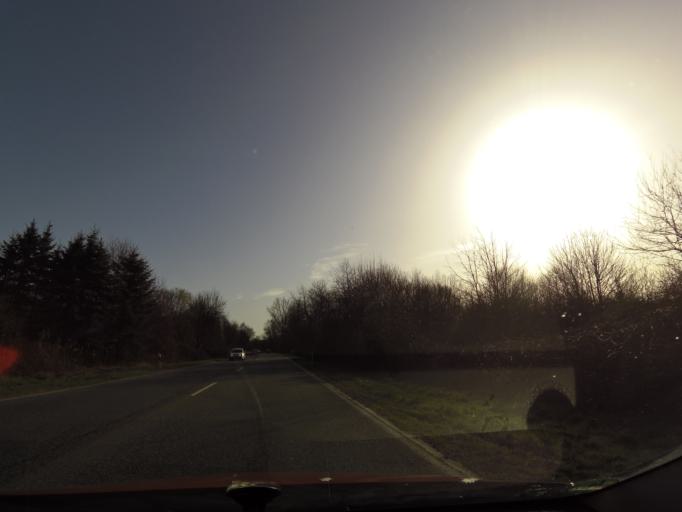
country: DE
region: Rheinland-Pfalz
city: Rheinbreitbach
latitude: 50.6146
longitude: 7.2192
